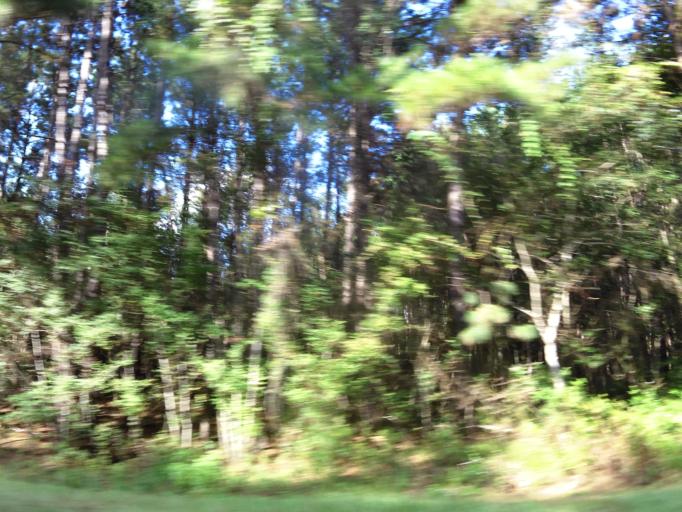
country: US
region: Georgia
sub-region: Brooks County
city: Quitman
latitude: 30.7854
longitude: -83.6313
